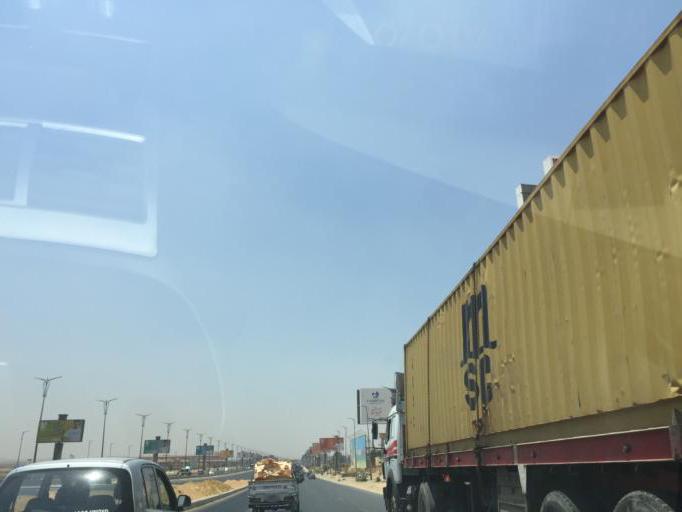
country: EG
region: Al Jizah
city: Awsim
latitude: 30.0518
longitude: 31.0451
